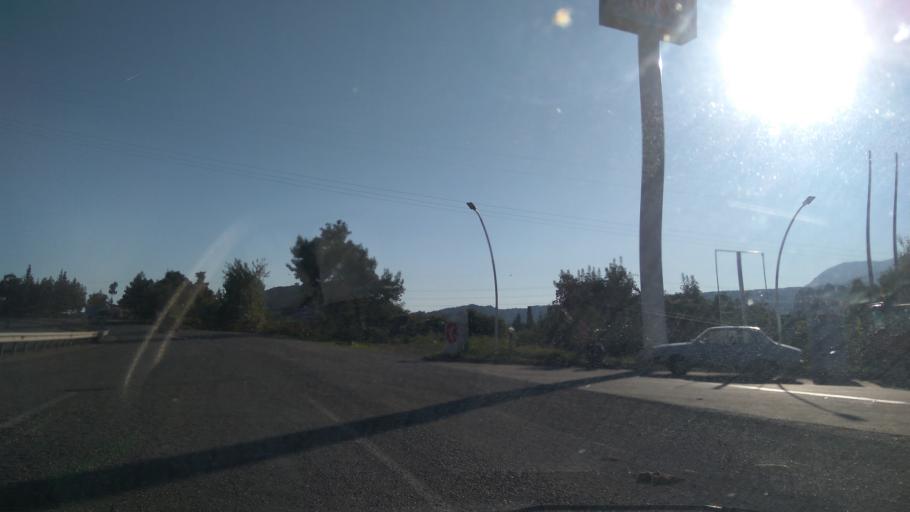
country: TR
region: Antalya
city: Kemer
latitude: 36.5860
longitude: 30.5424
